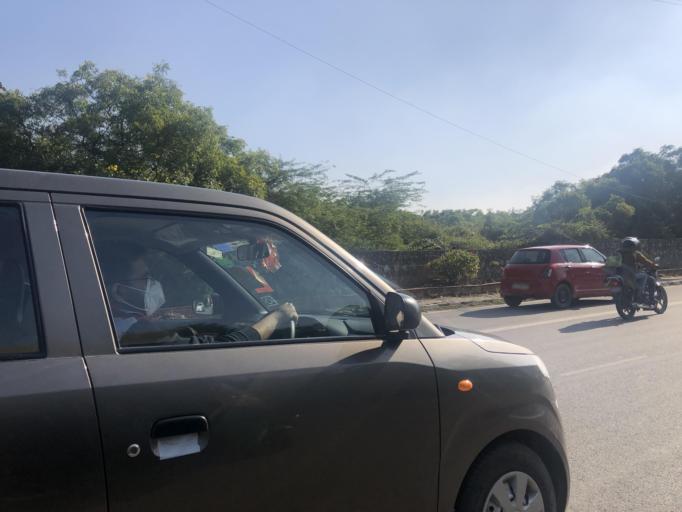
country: IN
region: NCT
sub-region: Central Delhi
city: Karol Bagh
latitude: 28.5515
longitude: 77.1650
